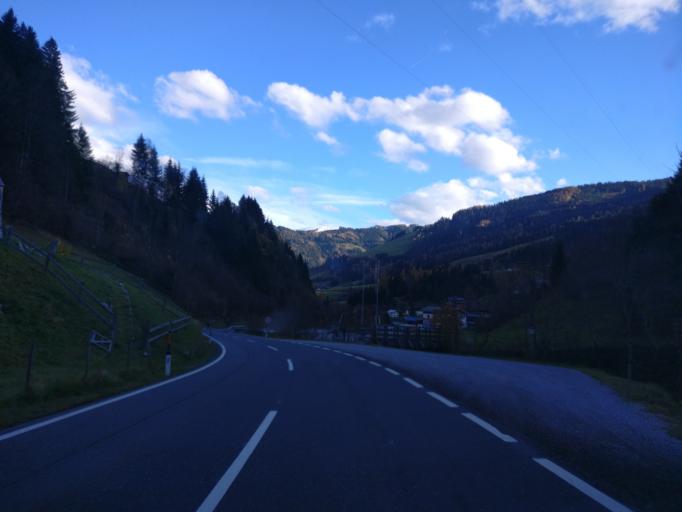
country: AT
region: Salzburg
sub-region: Politischer Bezirk Sankt Johann im Pongau
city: Muhlbach am Hochkonig
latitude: 47.3815
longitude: 13.1068
